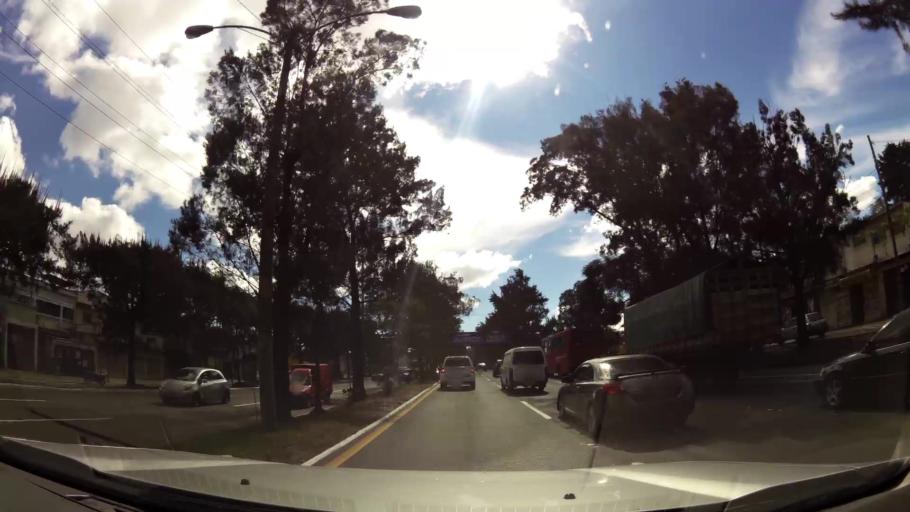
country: GT
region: Guatemala
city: Guatemala City
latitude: 14.6312
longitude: -90.5545
